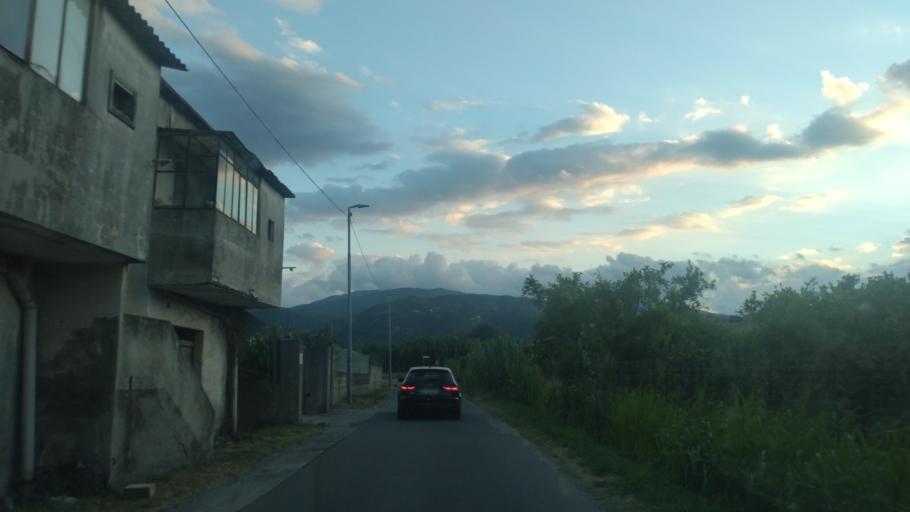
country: IT
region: Calabria
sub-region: Provincia di Catanzaro
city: Marina di Davoli
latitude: 38.6707
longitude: 16.5435
